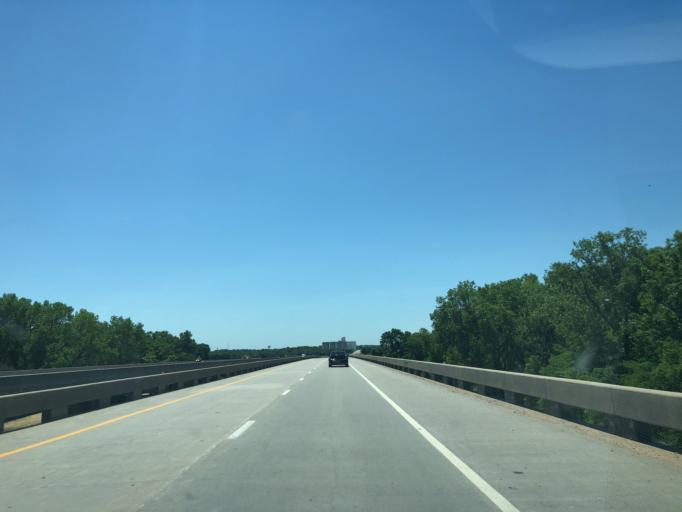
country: US
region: Kansas
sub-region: Cloud County
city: Concordia
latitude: 39.5912
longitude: -97.6590
